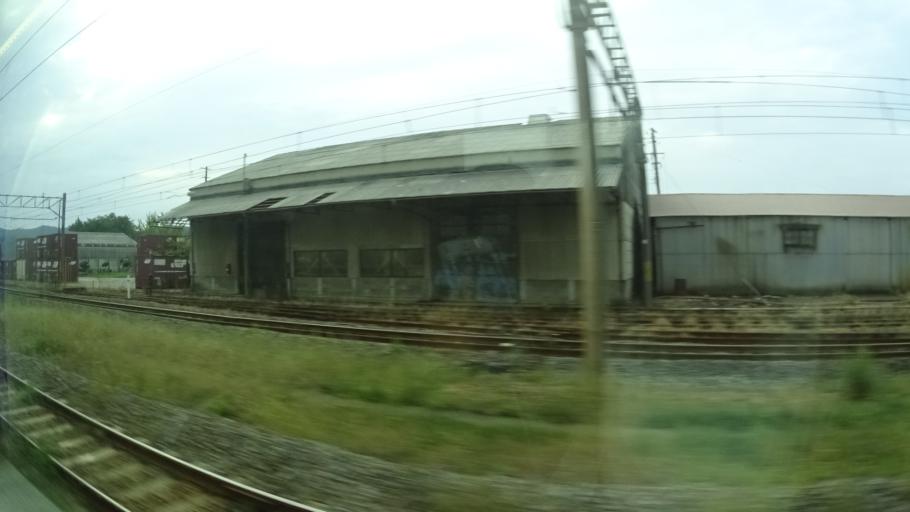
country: JP
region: Yamagata
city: Tsuruoka
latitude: 38.7148
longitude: 139.7339
